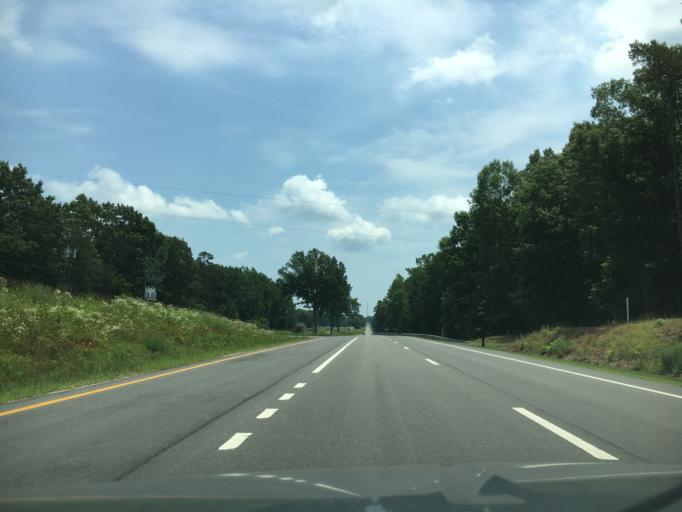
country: US
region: Virginia
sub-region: Buckingham County
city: Buckingham
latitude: 37.5438
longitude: -78.5166
